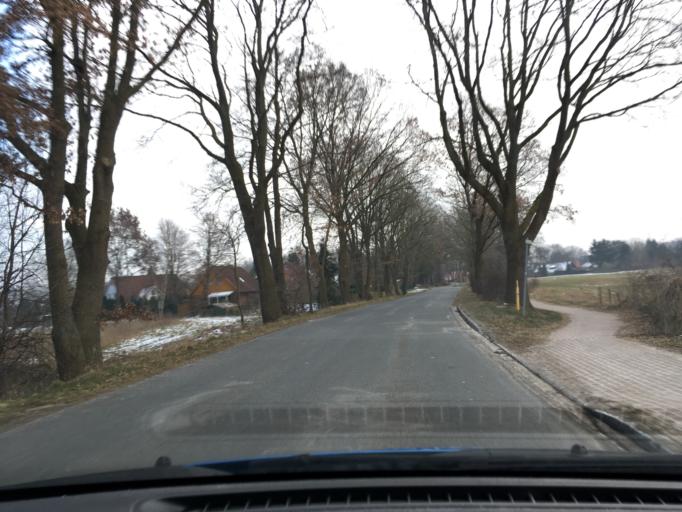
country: DE
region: Lower Saxony
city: Bienenbuttel
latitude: 53.1500
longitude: 10.4878
